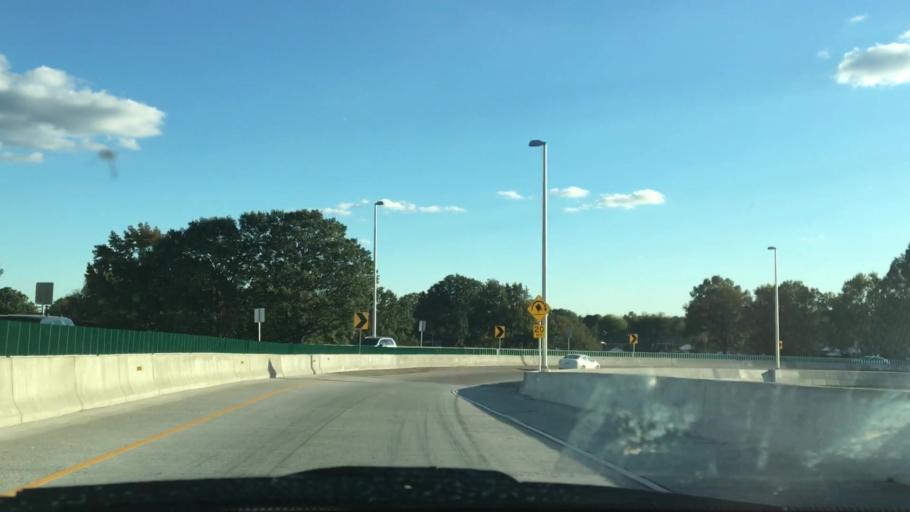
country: US
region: Virginia
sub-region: City of Portsmouth
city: Portsmouth
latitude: 36.8254
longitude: -76.3256
